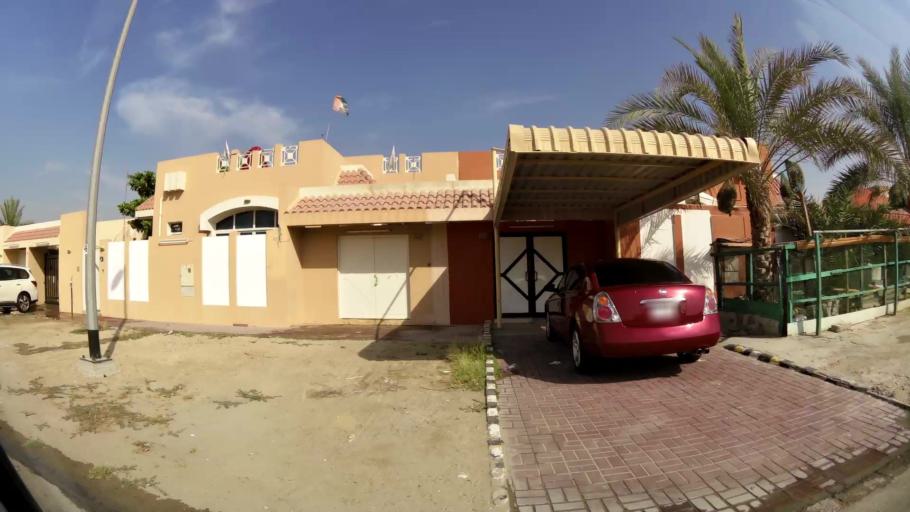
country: AE
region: Ash Shariqah
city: Sharjah
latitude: 25.2583
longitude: 55.3986
